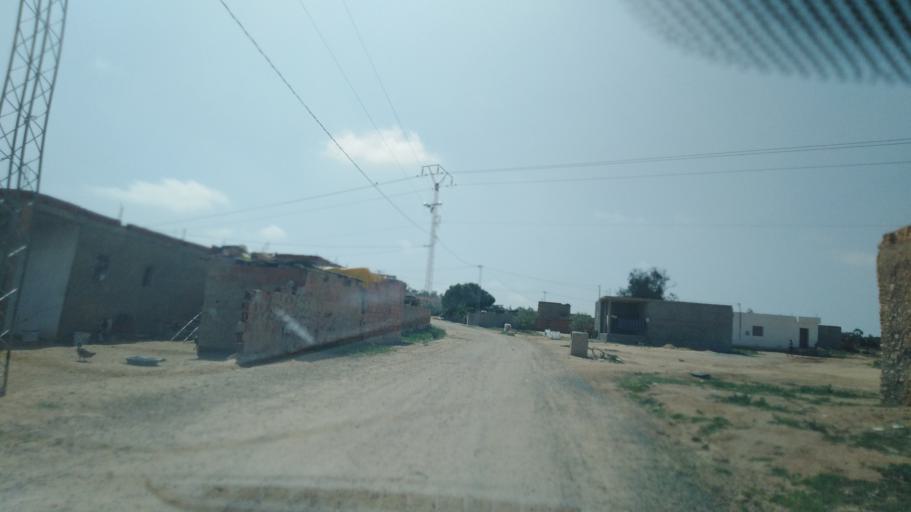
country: TN
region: Safaqis
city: Sfax
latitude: 34.7294
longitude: 10.5678
